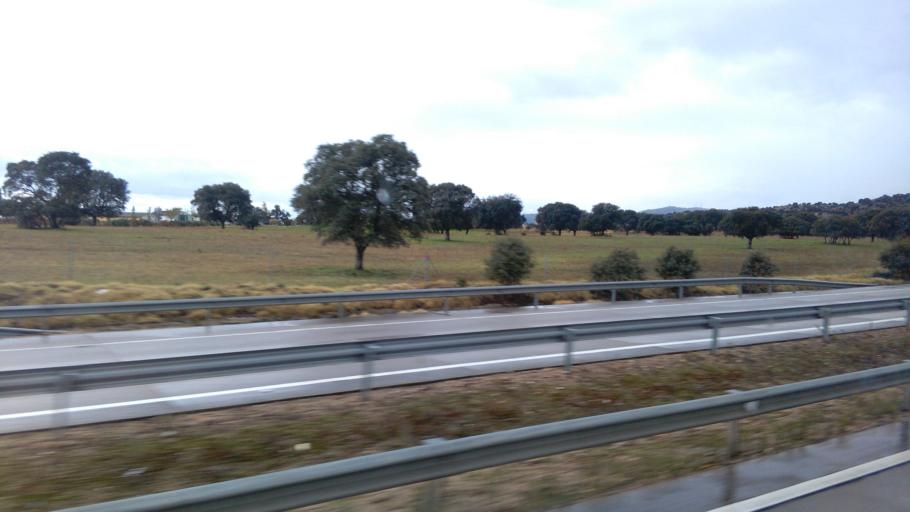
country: ES
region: Castille-La Mancha
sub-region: Province of Toledo
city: Cervera de los Montes
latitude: 40.0176
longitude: -4.7869
